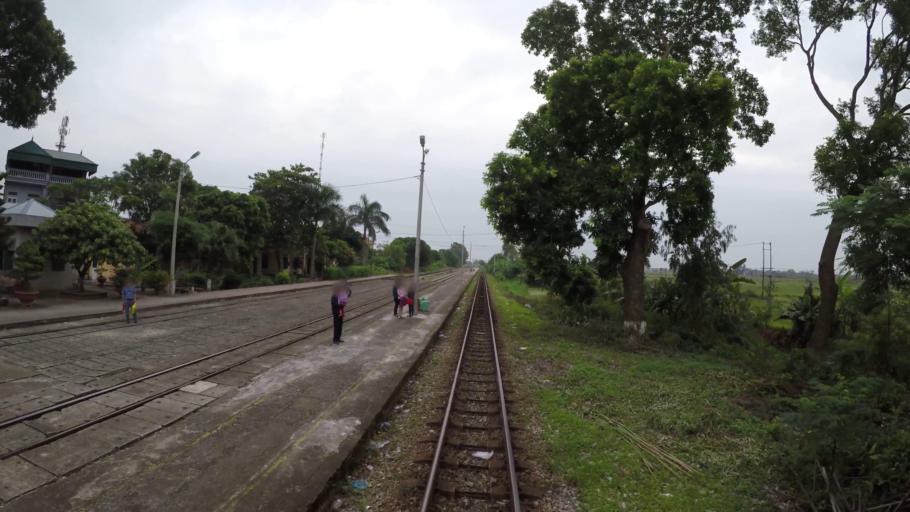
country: VN
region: Hai Duong
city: Ke Sat
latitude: 20.9666
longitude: 106.1500
